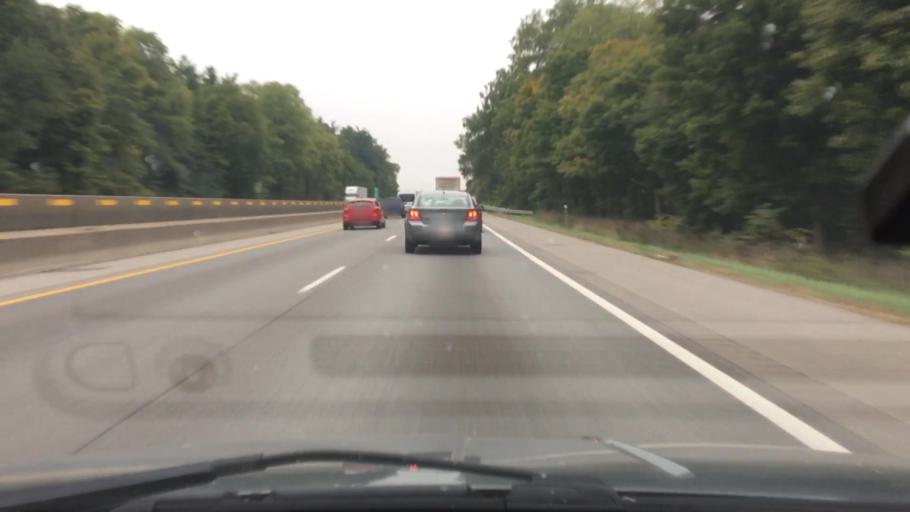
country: US
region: Michigan
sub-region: Kalamazoo County
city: Galesburg
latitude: 42.2758
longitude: -85.4178
